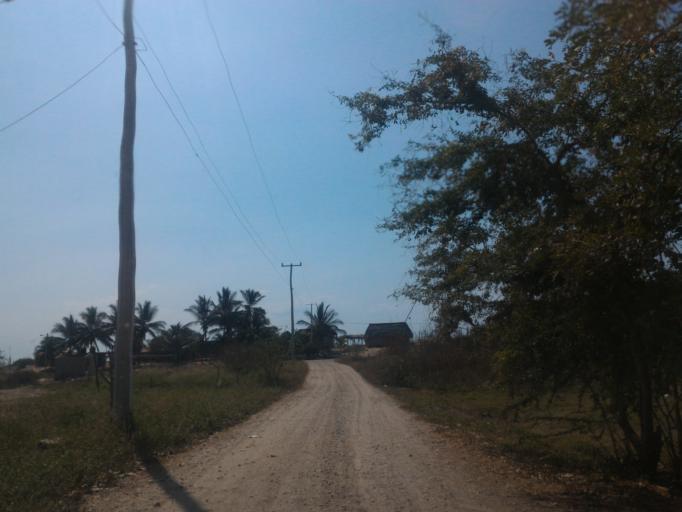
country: MX
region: Michoacan
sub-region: Coalcoman de Vazquez Pallares
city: Coalcoman de Vazquez Pallares
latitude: 18.2728
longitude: -103.3442
